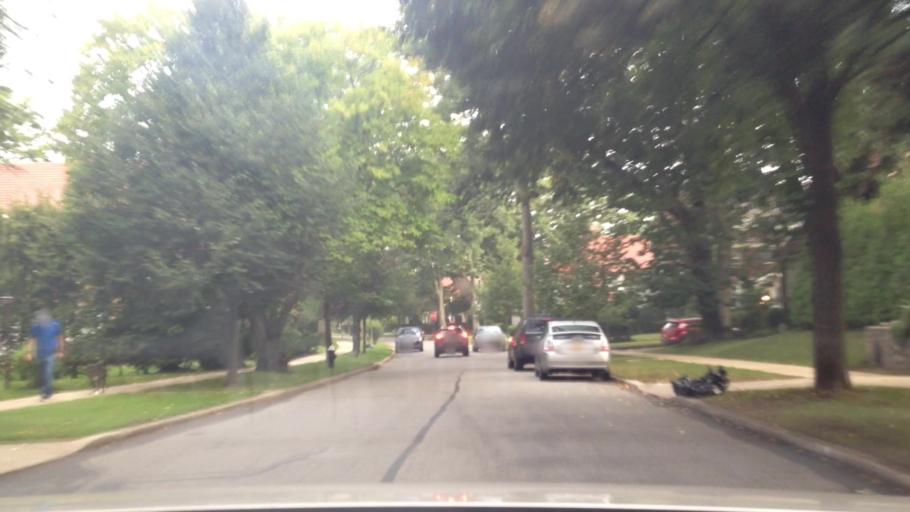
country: US
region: New York
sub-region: Queens County
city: Borough of Queens
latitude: 40.7117
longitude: -73.8404
